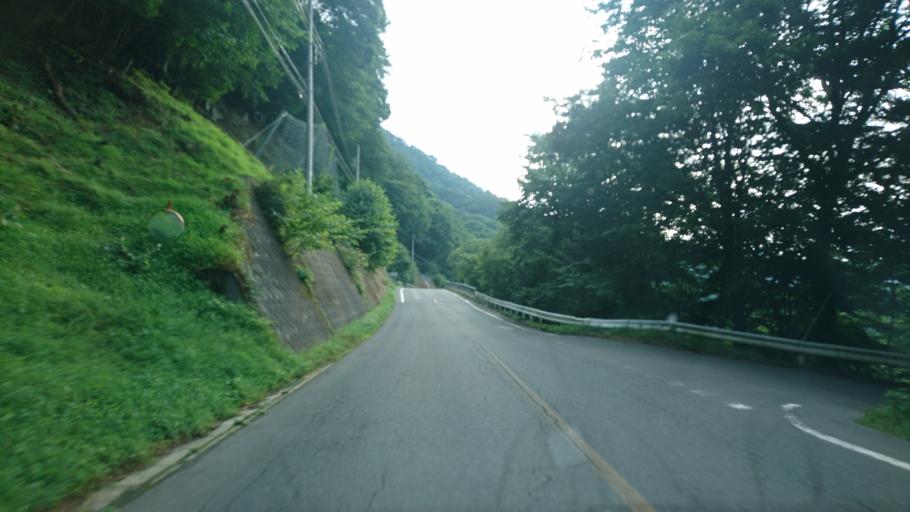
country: JP
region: Gunma
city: Numata
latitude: 36.6118
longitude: 139.2063
